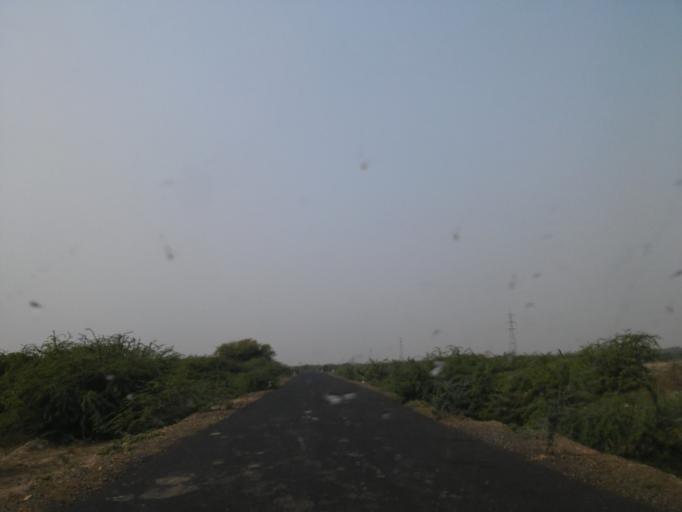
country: IN
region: Gujarat
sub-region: Kachchh
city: Bhuj
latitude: 23.6662
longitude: 69.6472
